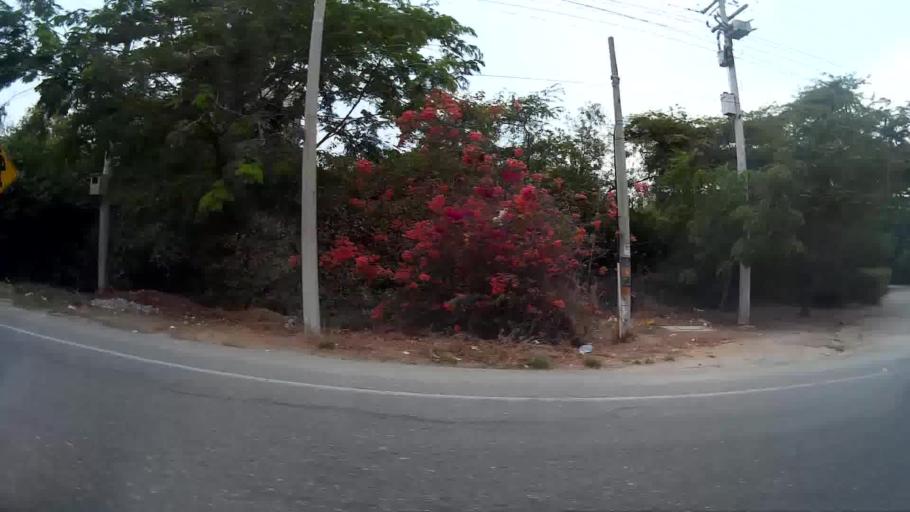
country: CO
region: Magdalena
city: Santa Marta
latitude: 11.1484
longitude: -74.2214
